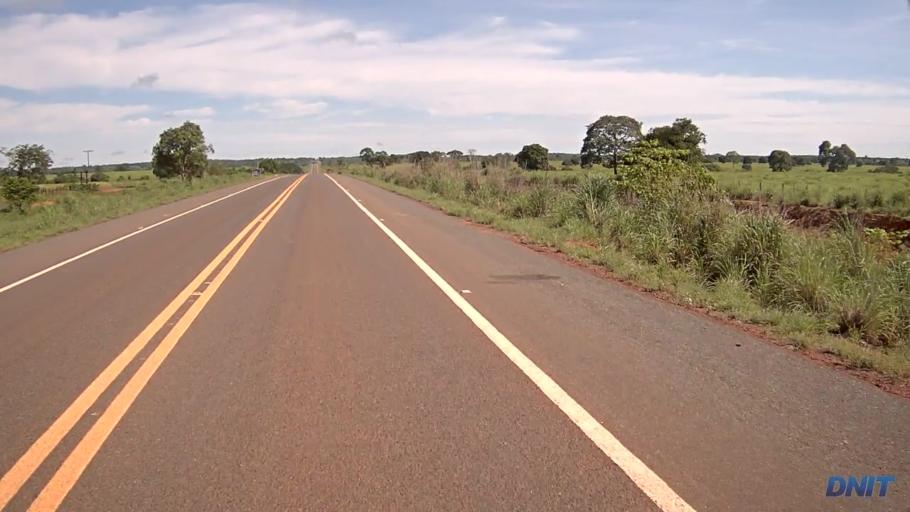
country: BR
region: Goias
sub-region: Sao Miguel Do Araguaia
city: Sao Miguel do Araguaia
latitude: -13.3702
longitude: -50.1438
